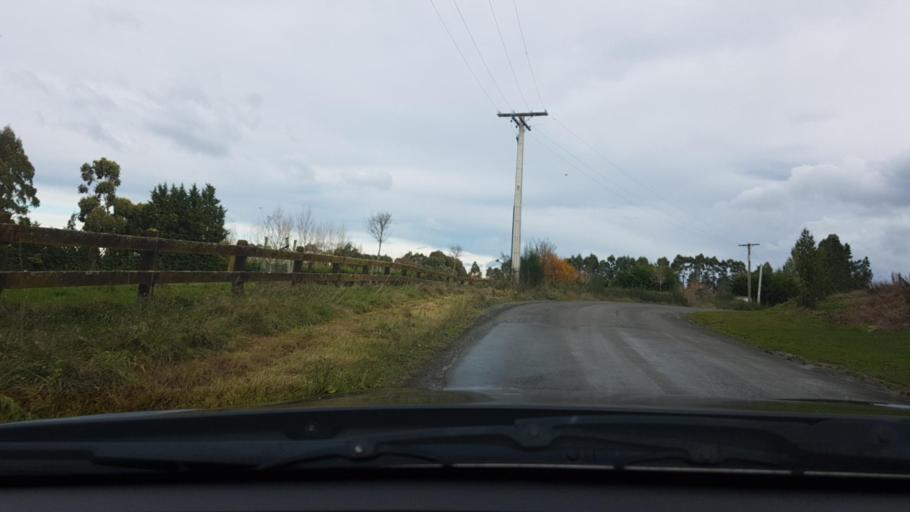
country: NZ
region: Canterbury
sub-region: Waimakariri District
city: Oxford
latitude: -43.2925
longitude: 172.1785
